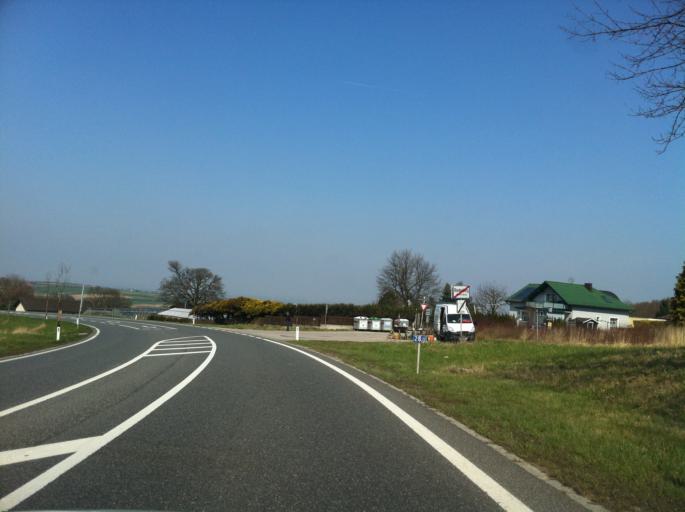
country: AT
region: Lower Austria
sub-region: Politischer Bezirk Tulln
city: Tulbing
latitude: 48.2542
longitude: 16.0886
